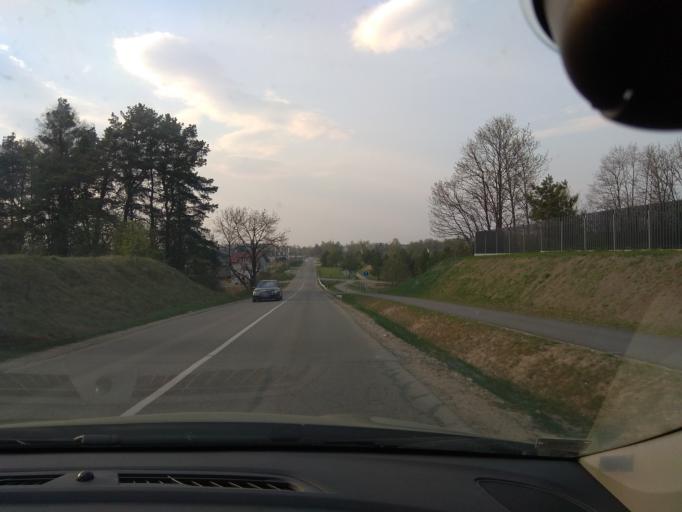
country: LT
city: Grigiskes
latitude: 54.6198
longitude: 25.1147
